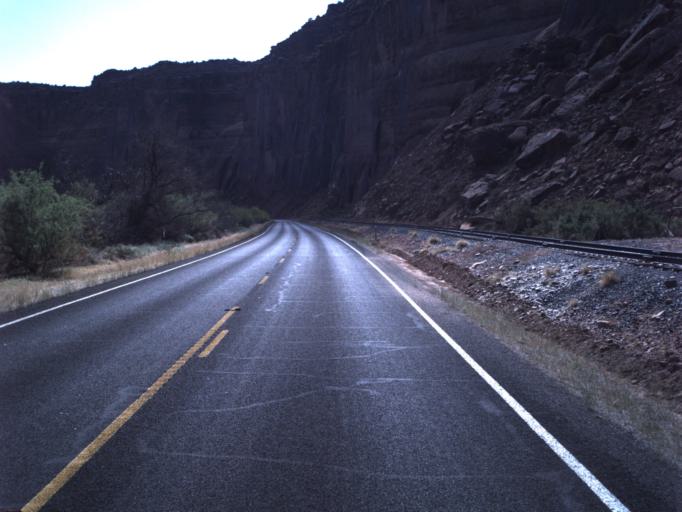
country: US
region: Utah
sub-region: Grand County
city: Moab
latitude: 38.5713
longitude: -109.6556
